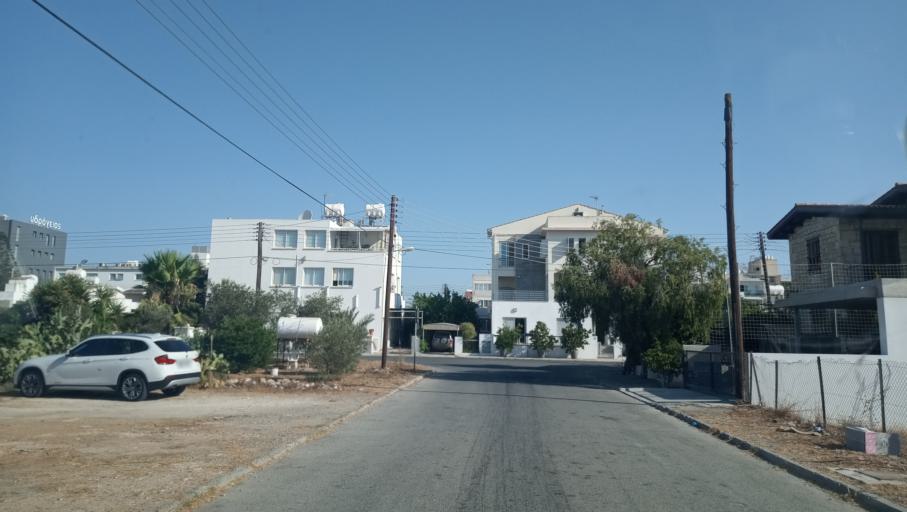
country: CY
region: Lefkosia
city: Nicosia
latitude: 35.1475
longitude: 33.3876
